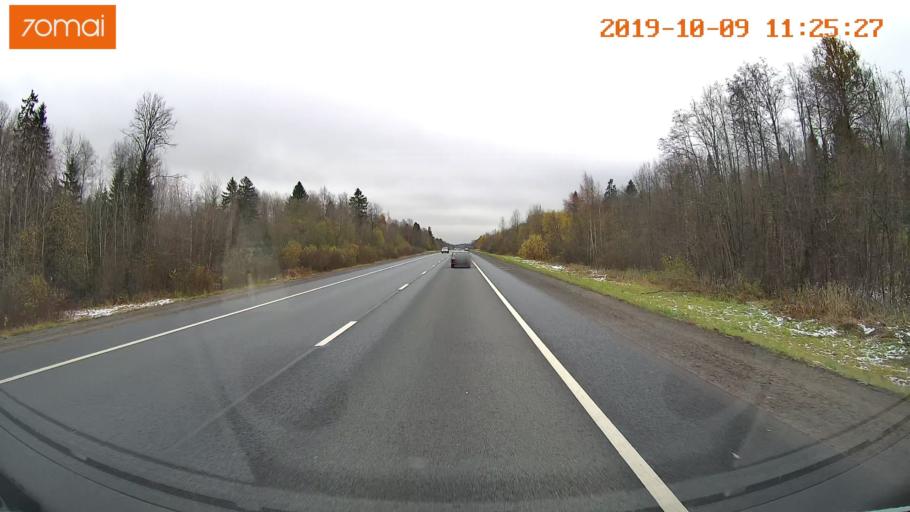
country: RU
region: Vologda
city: Vologda
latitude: 59.1006
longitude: 39.9918
